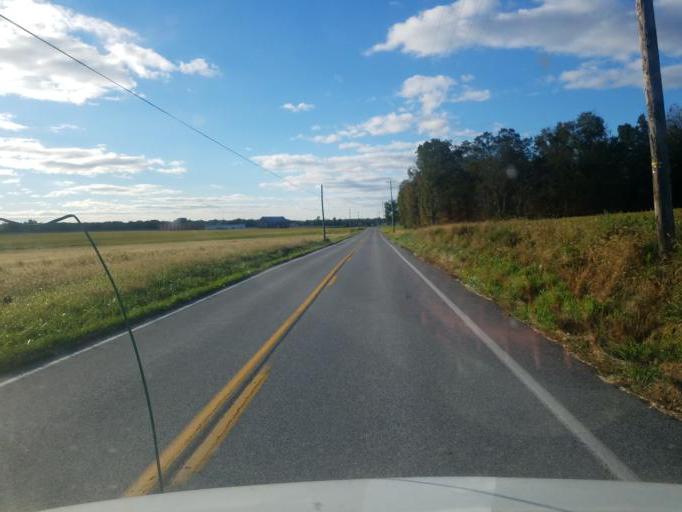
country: US
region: Pennsylvania
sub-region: Adams County
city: Gettysburg
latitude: 39.8671
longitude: -77.2291
